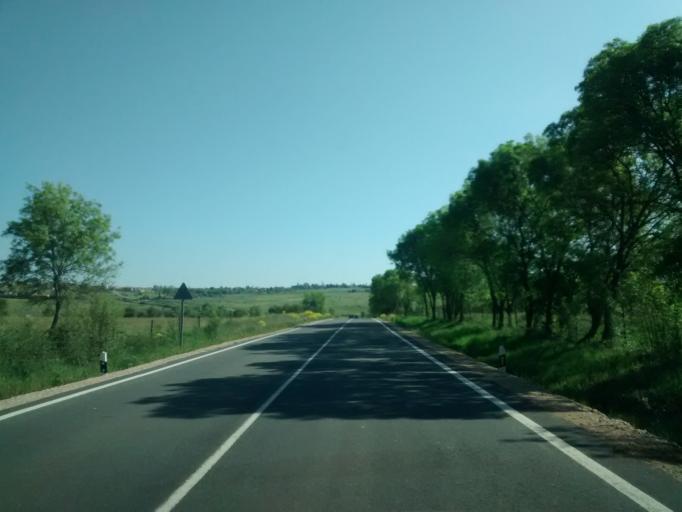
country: ES
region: Castille and Leon
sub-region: Provincia de Segovia
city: Trescasas
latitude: 40.9758
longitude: -4.0263
